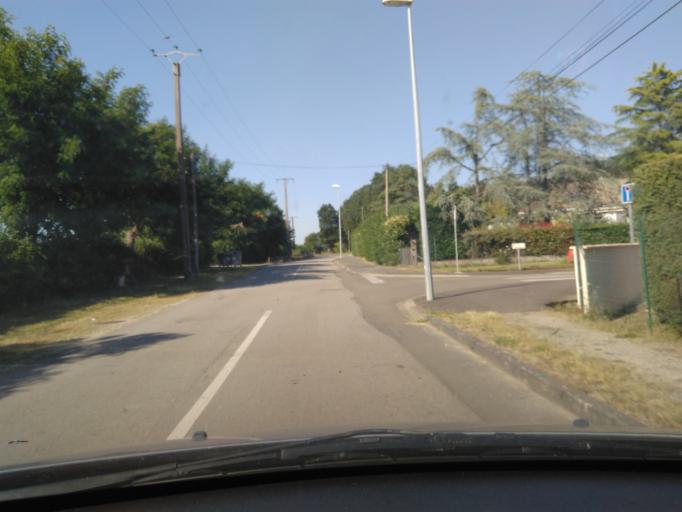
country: FR
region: Pays de la Loire
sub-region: Departement de la Vendee
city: Mouilleron-le-Captif
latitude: 46.7298
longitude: -1.4215
